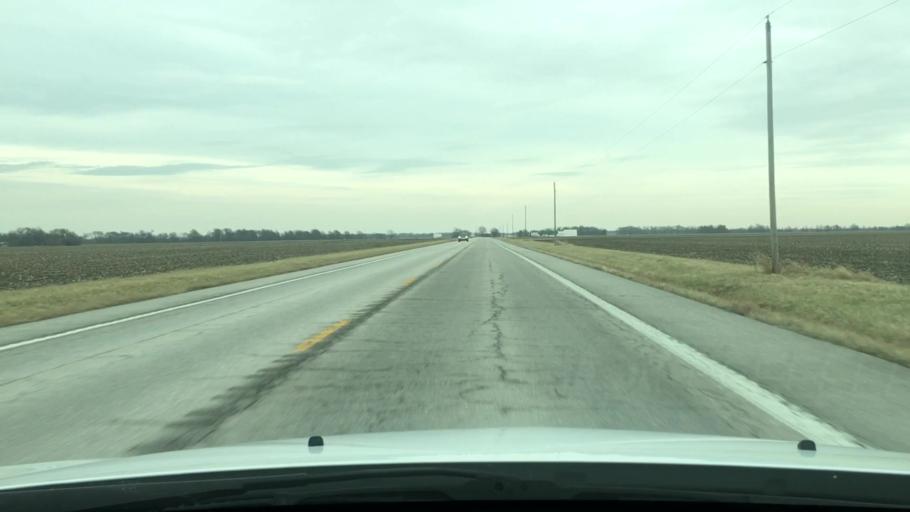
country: US
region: Missouri
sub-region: Audrain County
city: Vandalia
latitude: 39.2809
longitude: -91.6338
